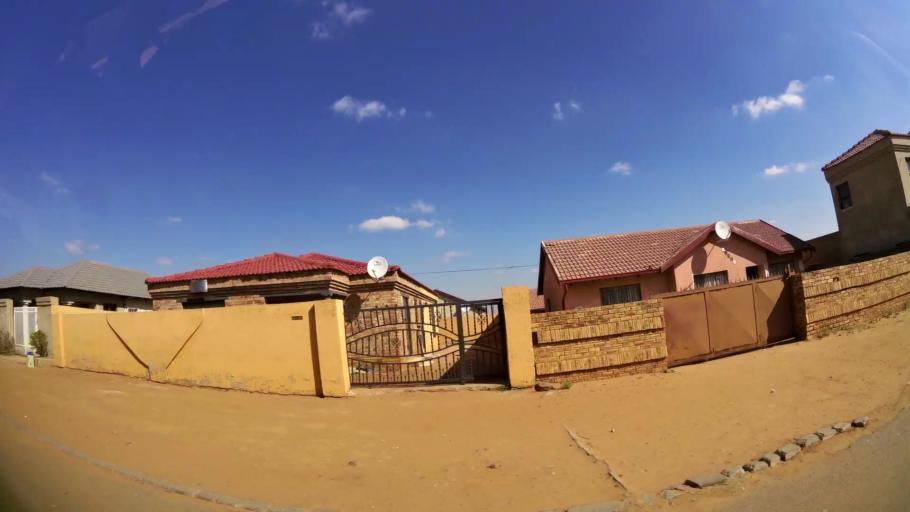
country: ZA
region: Gauteng
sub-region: West Rand District Municipality
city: Krugersdorp
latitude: -26.1455
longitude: 27.7719
